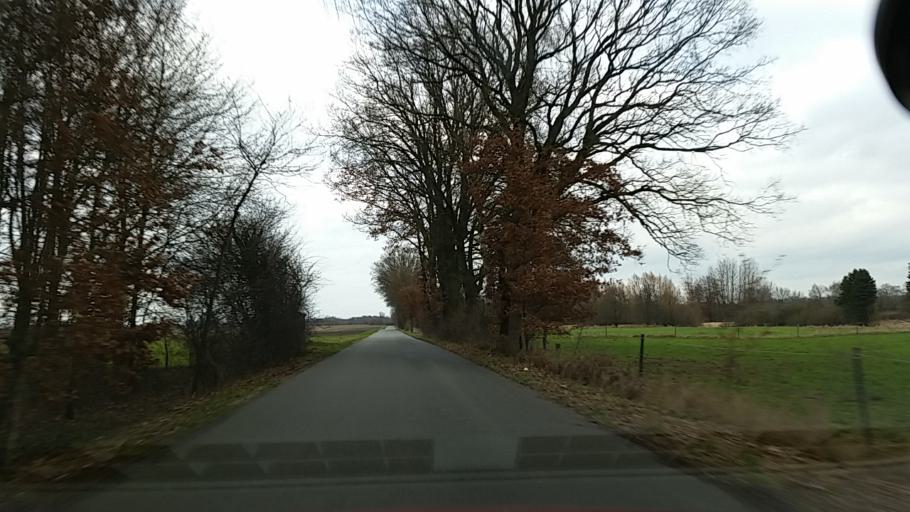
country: DE
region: Lower Saxony
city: Luder
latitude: 52.8143
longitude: 10.6676
